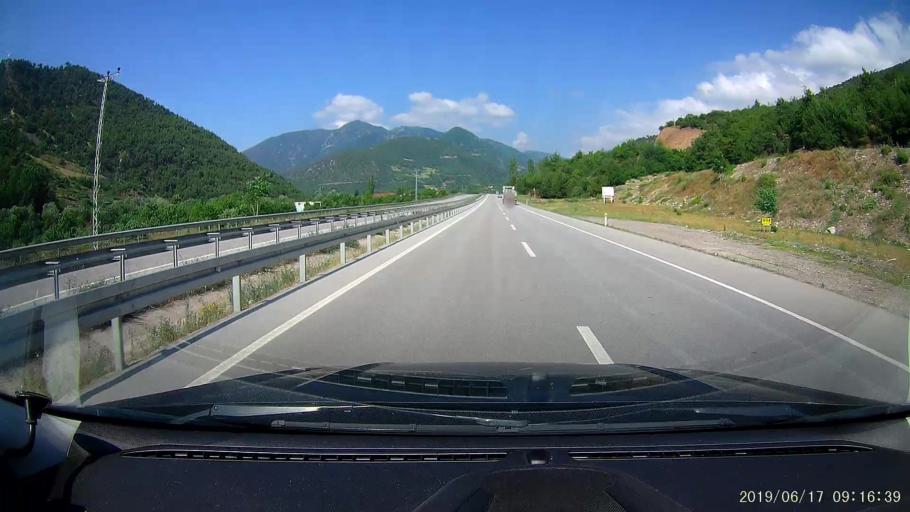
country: TR
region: Amasya
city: Akdag
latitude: 40.7445
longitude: 36.0052
